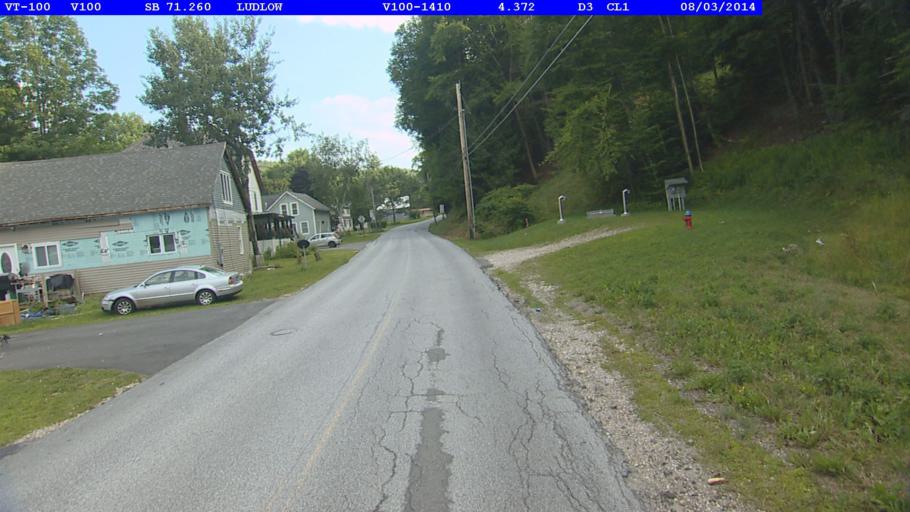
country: US
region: Vermont
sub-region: Windsor County
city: Chester
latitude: 43.3881
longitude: -72.7093
